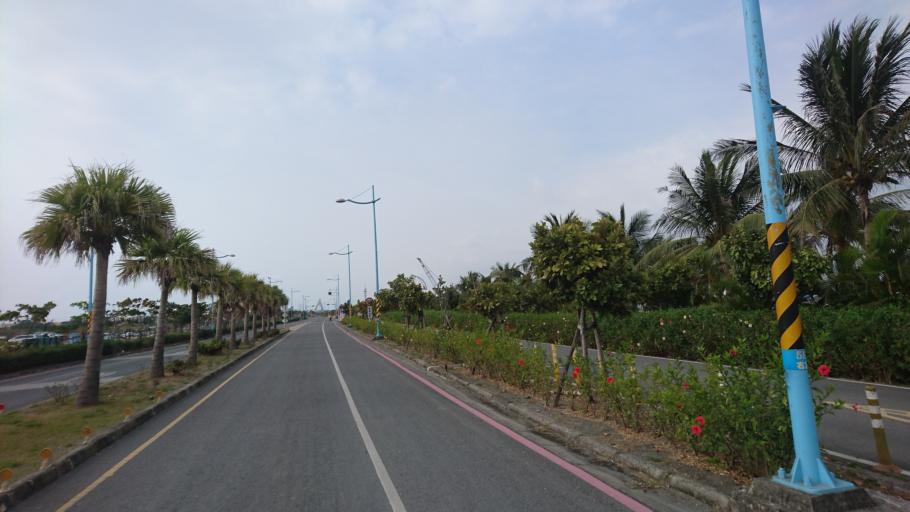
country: TW
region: Taiwan
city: Fengshan
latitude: 22.4364
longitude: 120.4769
